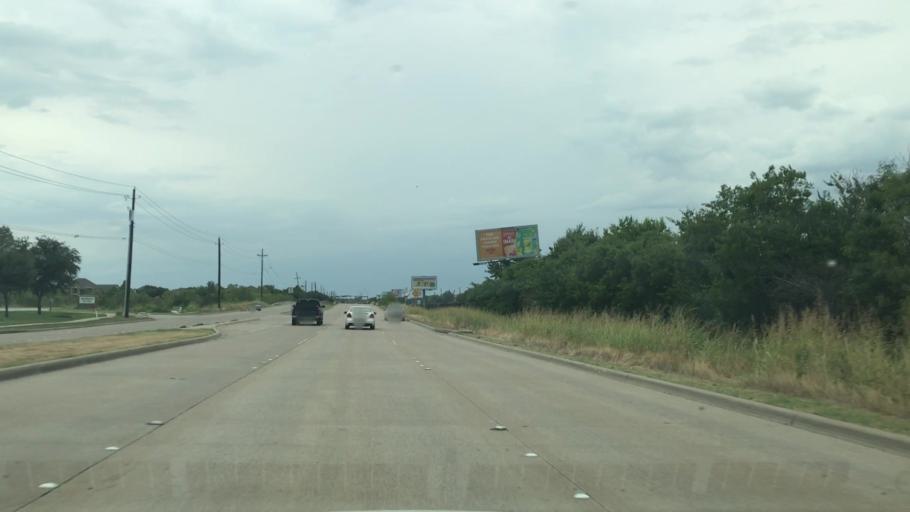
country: US
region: Texas
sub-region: Dallas County
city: Carrollton
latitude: 32.9519
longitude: -96.9435
